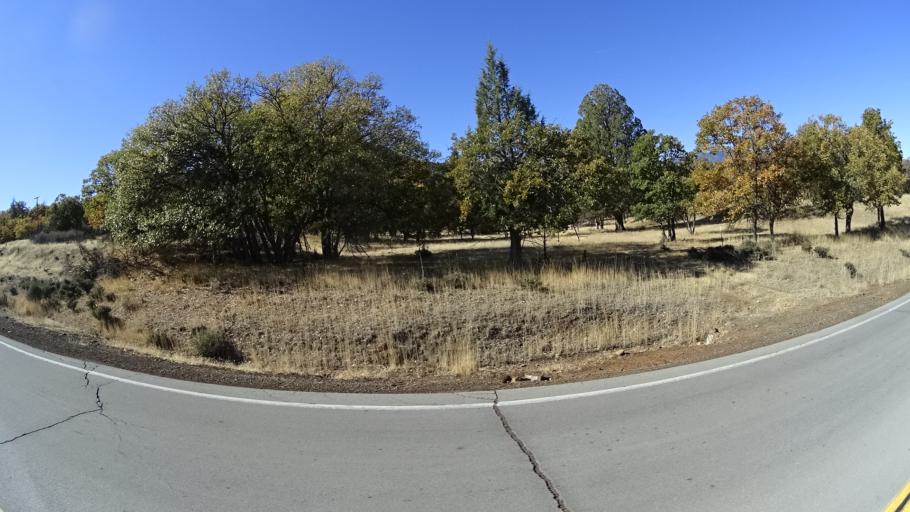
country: US
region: California
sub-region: Siskiyou County
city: Montague
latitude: 41.8856
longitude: -122.4865
